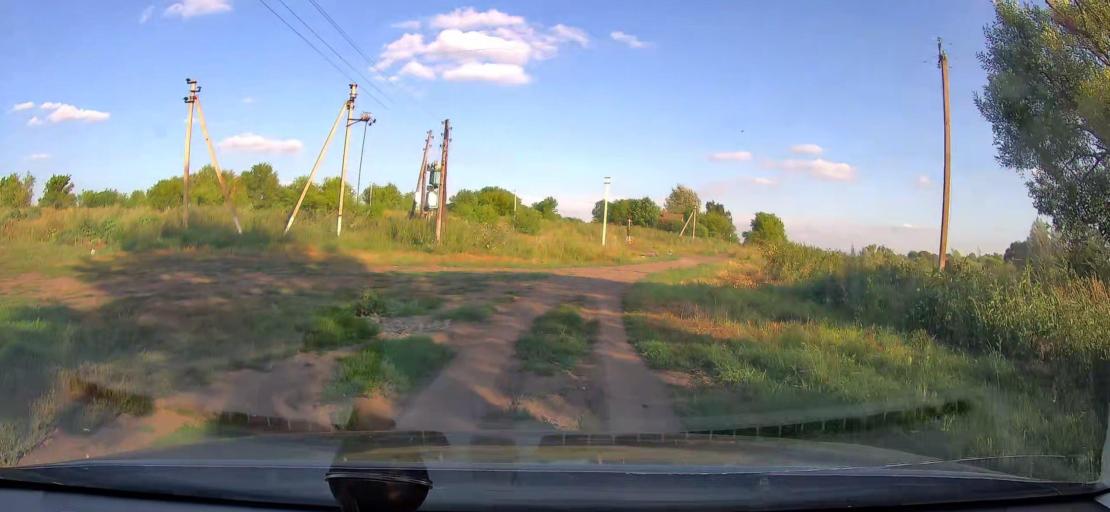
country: RU
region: Kursk
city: Zolotukhino
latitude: 52.0256
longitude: 36.2051
